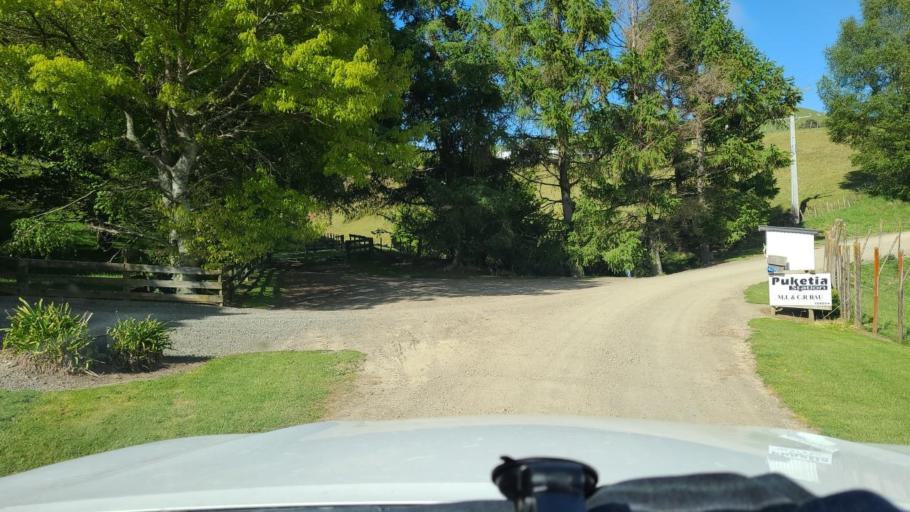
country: NZ
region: Bay of Plenty
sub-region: Opotiki District
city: Opotiki
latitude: -38.4619
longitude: 177.3835
